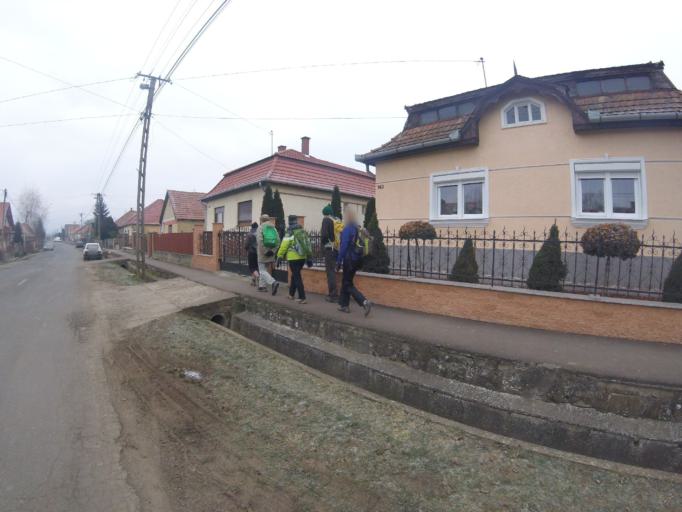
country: HU
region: Nograd
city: Paszto
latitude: 47.9506
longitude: 19.6938
